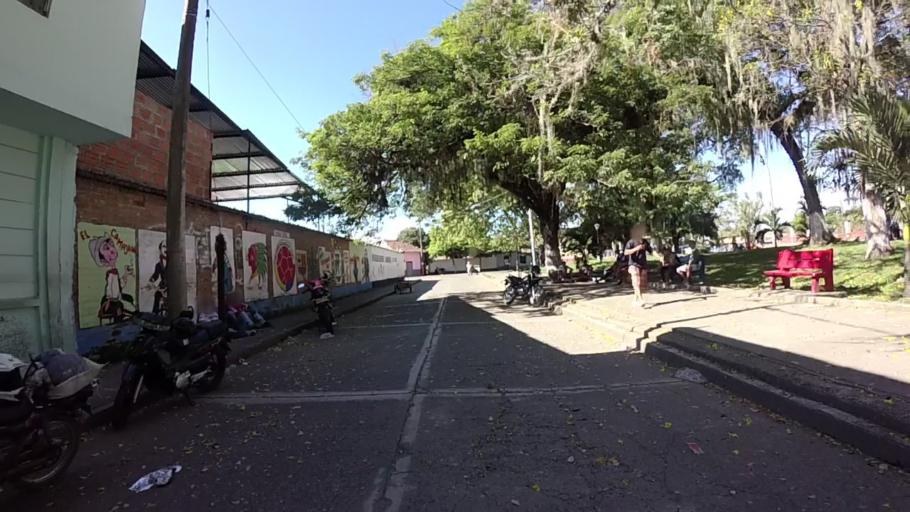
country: CO
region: Valle del Cauca
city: Cartago
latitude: 4.7461
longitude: -75.9077
